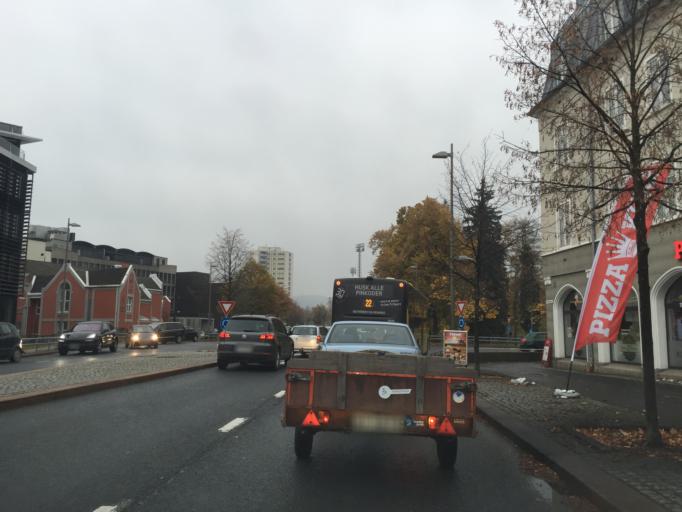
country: NO
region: Buskerud
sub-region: Drammen
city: Drammen
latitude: 59.7396
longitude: 10.1985
